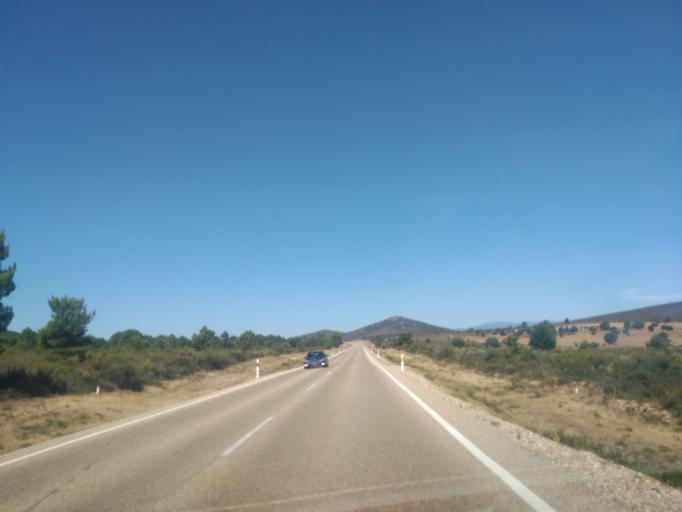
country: ES
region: Castille and Leon
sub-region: Provincia de Zamora
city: Otero de Bodas
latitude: 41.9322
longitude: -6.1197
